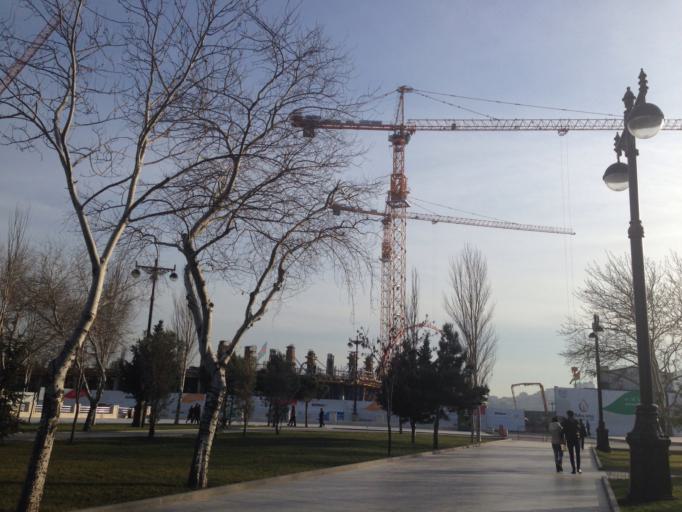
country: AZ
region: Baki
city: Badamdar
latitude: 40.3597
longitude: 49.8364
